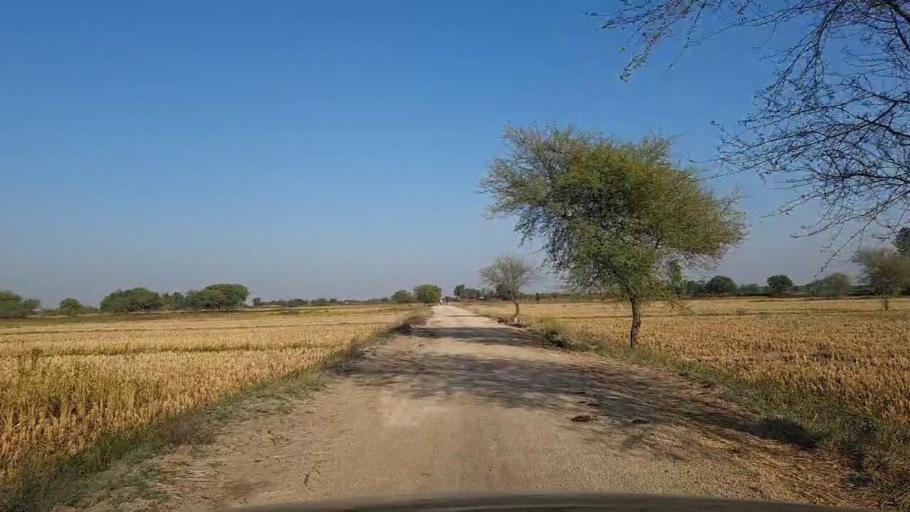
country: PK
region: Sindh
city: Mirpur Batoro
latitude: 24.6837
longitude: 68.3615
